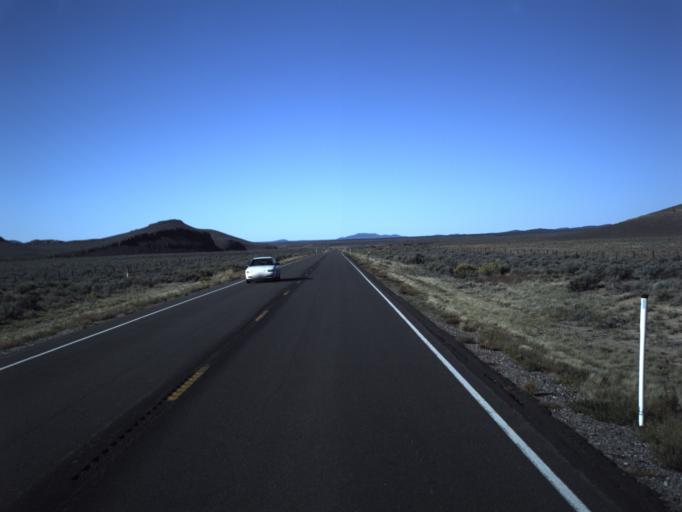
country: US
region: Utah
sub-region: Washington County
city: Enterprise
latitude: 37.7978
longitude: -113.9356
